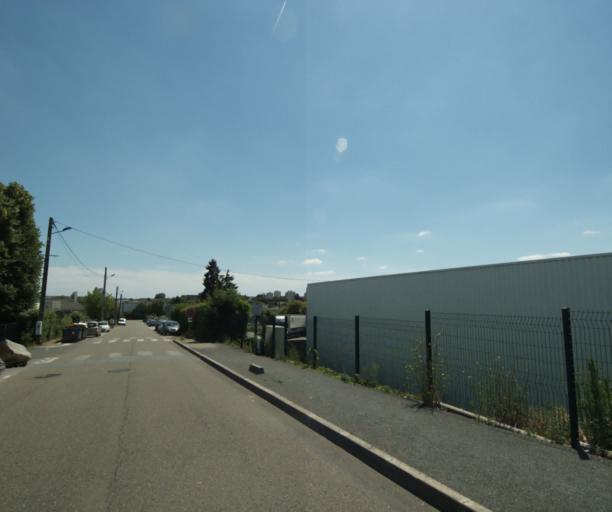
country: FR
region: Pays de la Loire
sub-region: Departement de la Mayenne
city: Laval
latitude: 48.0806
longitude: -0.7515
